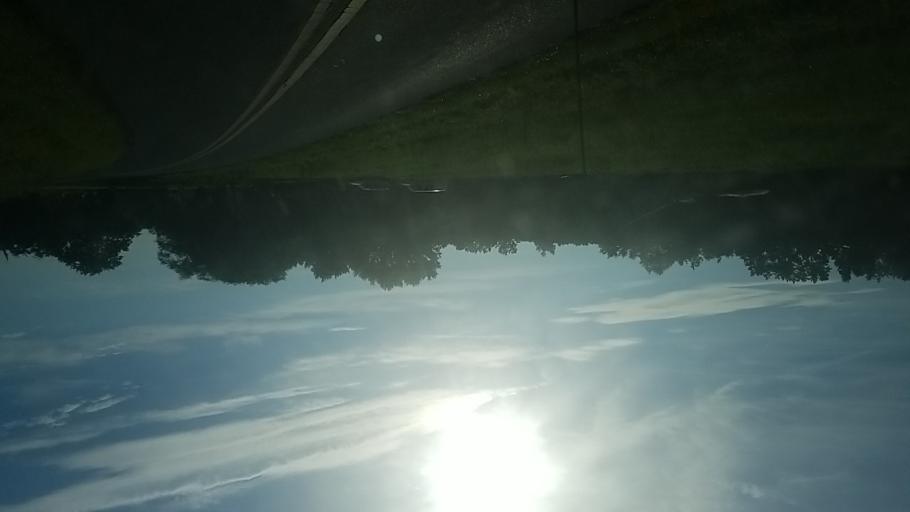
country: US
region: Maryland
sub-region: Worcester County
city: Berlin
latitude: 38.3140
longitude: -75.1631
